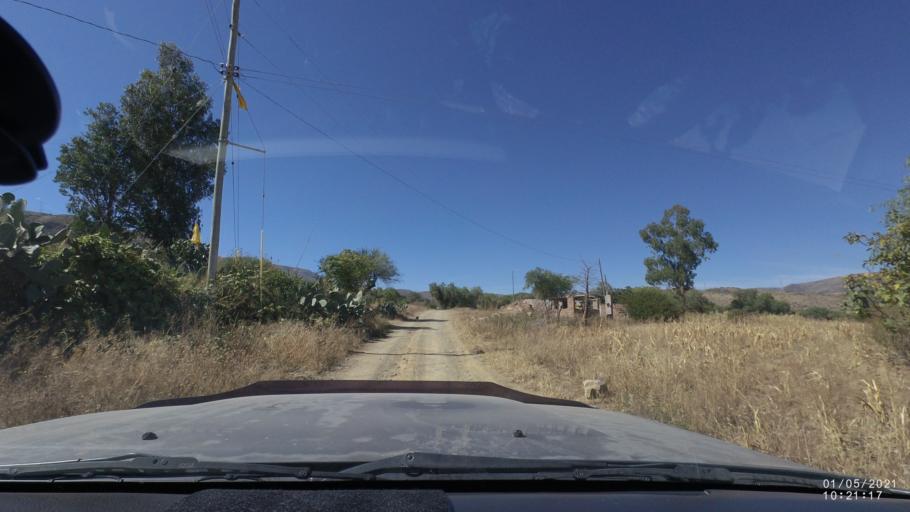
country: BO
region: Cochabamba
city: Capinota
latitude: -17.5644
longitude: -66.2022
